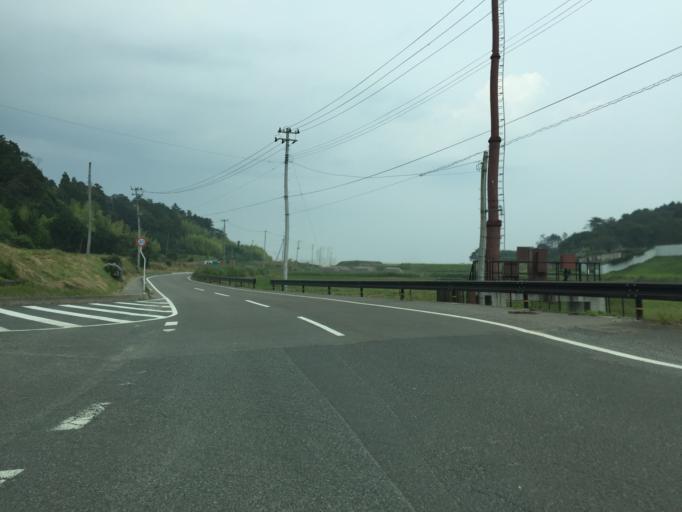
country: JP
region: Fukushima
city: Namie
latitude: 37.6528
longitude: 141.0149
